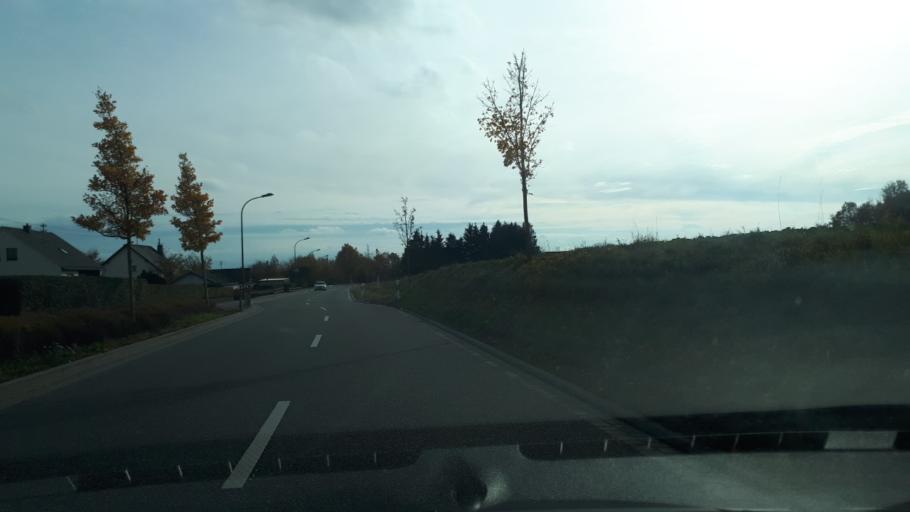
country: DE
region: Rheinland-Pfalz
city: Laubach
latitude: 50.2296
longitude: 7.0725
